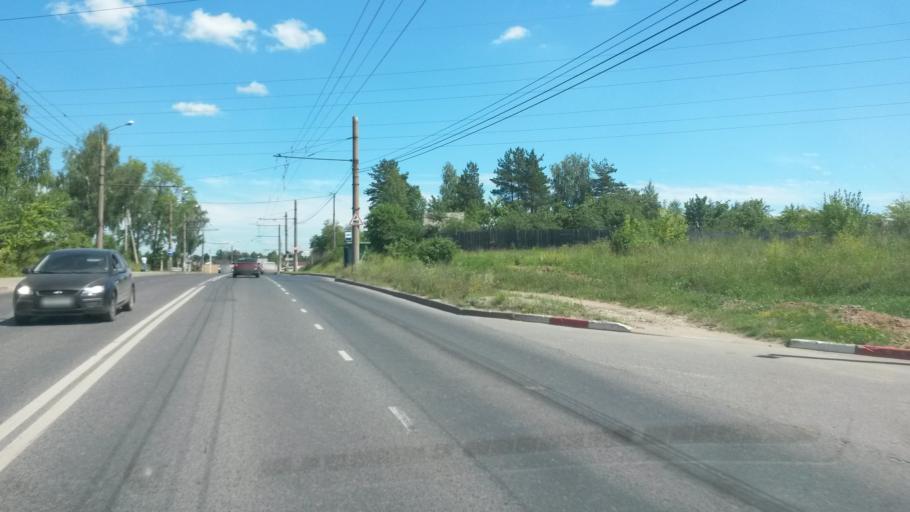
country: RU
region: Ivanovo
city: Kokhma
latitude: 56.9637
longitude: 41.0346
